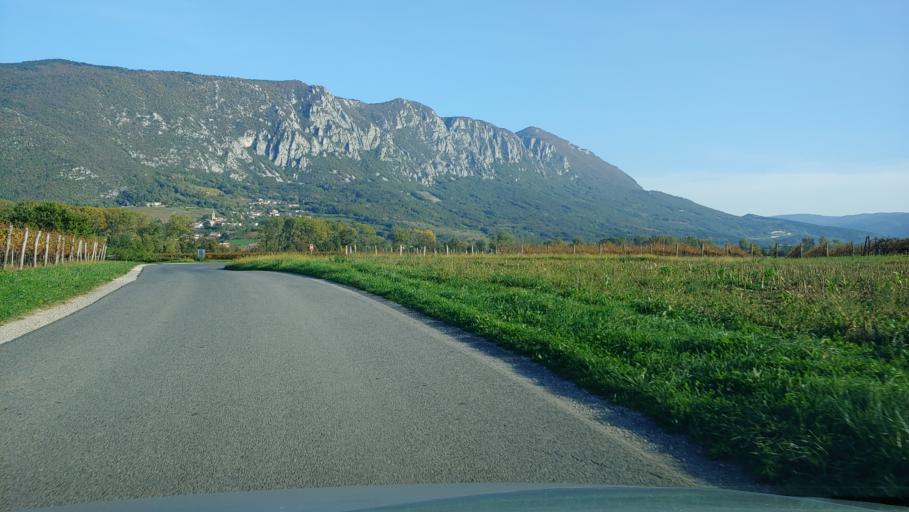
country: SI
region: Vipava
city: Vipava
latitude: 45.8400
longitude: 13.9415
